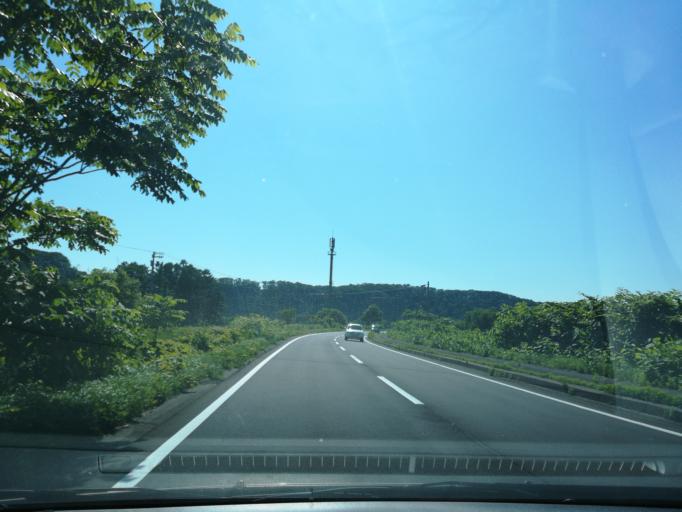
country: JP
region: Hokkaido
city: Chitose
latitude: 42.9084
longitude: 141.9309
